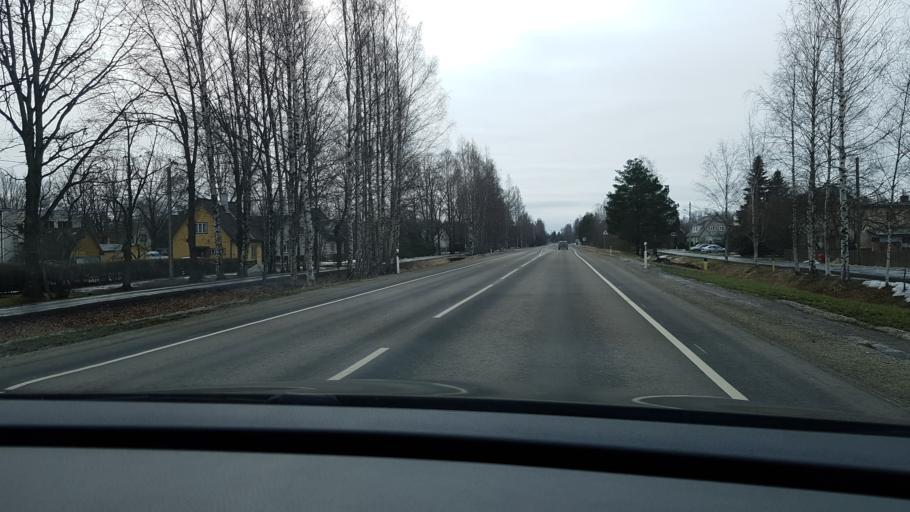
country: EE
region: Paernumaa
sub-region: Sindi linn
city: Sindi
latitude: 58.3986
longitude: 24.6491
